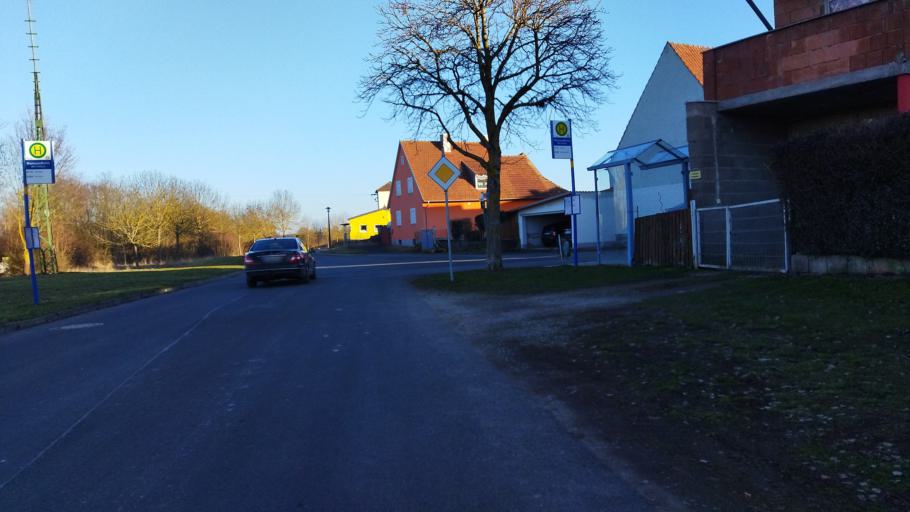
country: DE
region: Bavaria
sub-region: Regierungsbezirk Unterfranken
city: Dettelbach
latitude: 49.7960
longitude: 10.1717
